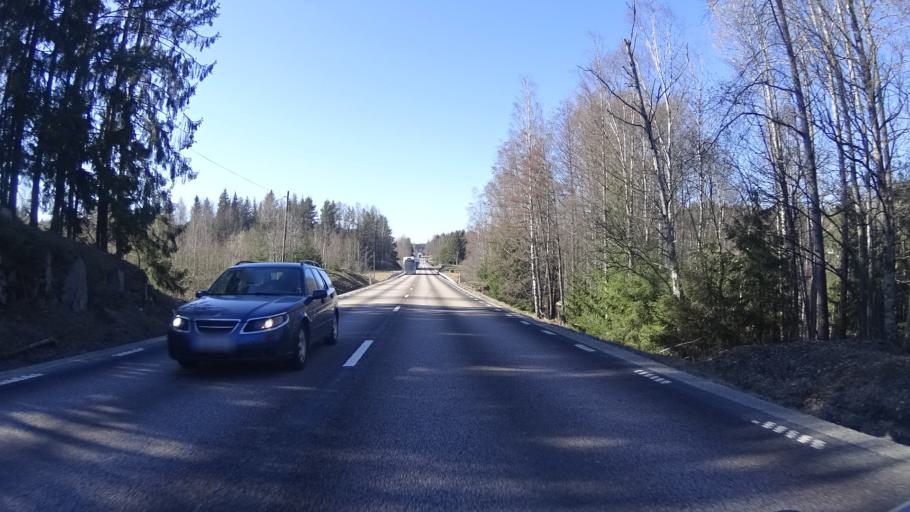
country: SE
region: Vaermland
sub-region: Sunne Kommun
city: Sunne
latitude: 59.6613
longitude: 12.9276
